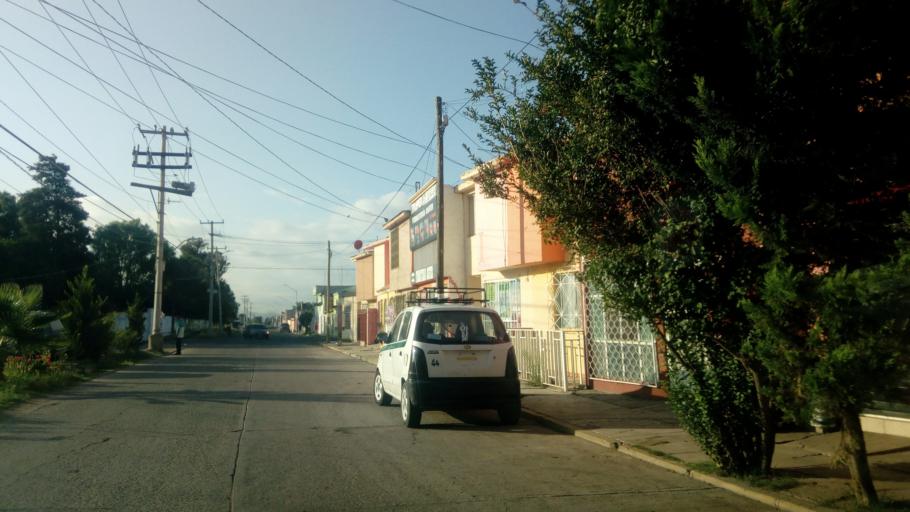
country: MX
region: Durango
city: Victoria de Durango
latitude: 24.0491
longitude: -104.6169
